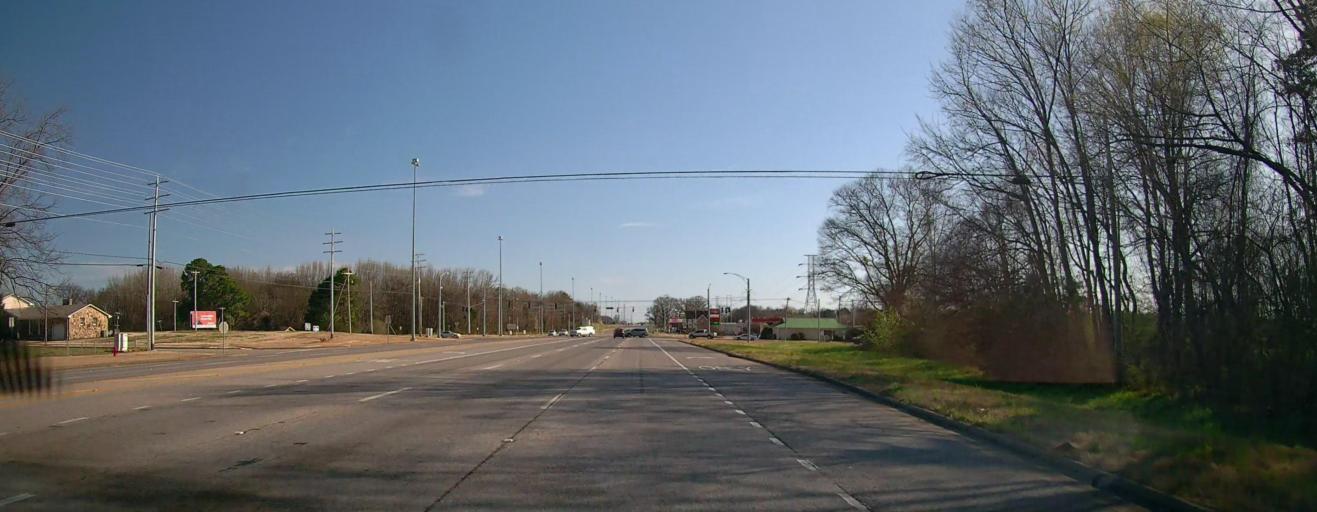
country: US
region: Alabama
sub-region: Colbert County
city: Muscle Shoals
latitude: 34.7604
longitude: -87.6349
